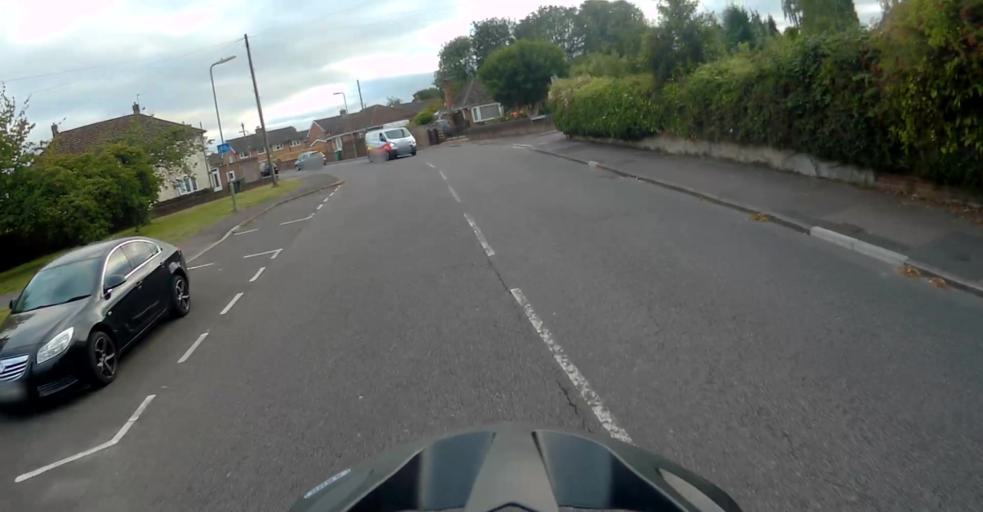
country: GB
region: England
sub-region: Hampshire
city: Basingstoke
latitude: 51.2611
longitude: -1.1208
